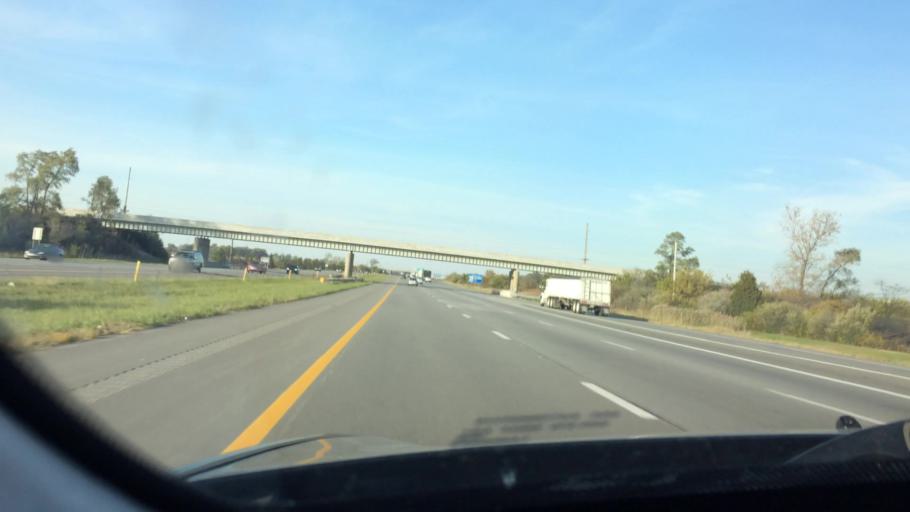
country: US
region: Ohio
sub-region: Wood County
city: Bowling Green
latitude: 41.3549
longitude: -83.6215
